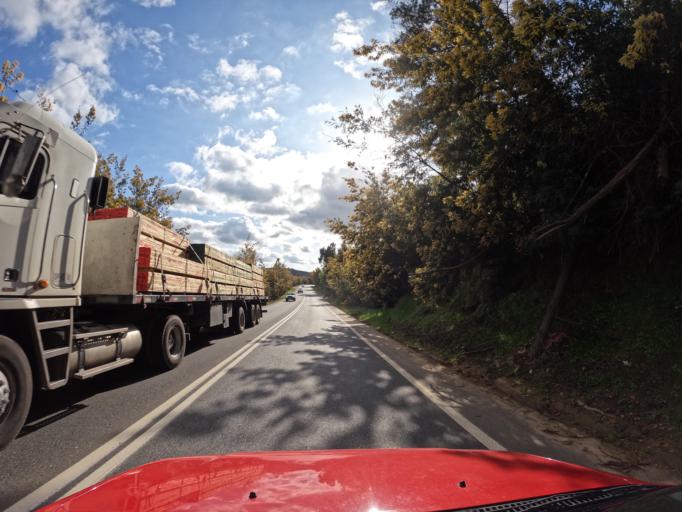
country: CL
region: Maule
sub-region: Provincia de Talca
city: Constitucion
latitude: -35.5373
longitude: -72.1618
